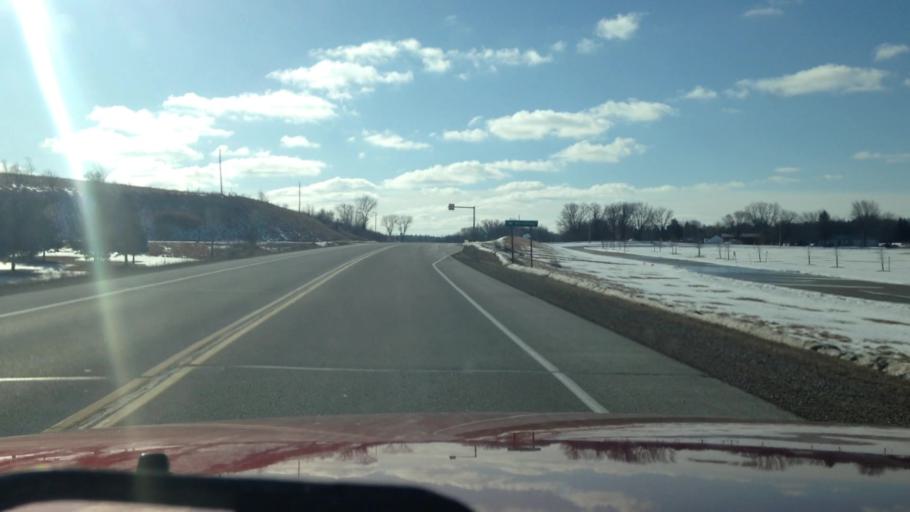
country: US
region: Wisconsin
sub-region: Waukesha County
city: Oconomowoc
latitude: 43.1685
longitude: -88.5031
